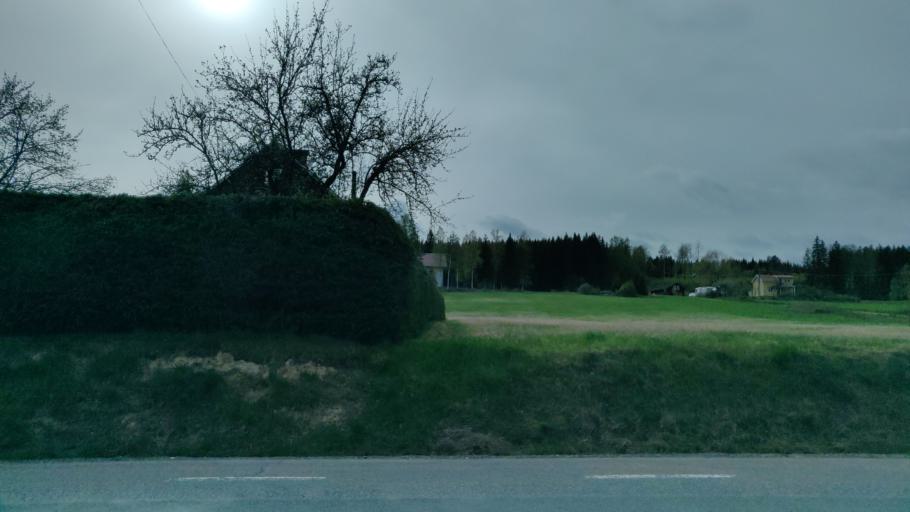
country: SE
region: Vaermland
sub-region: Munkfors Kommun
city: Munkfors
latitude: 59.8091
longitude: 13.5071
